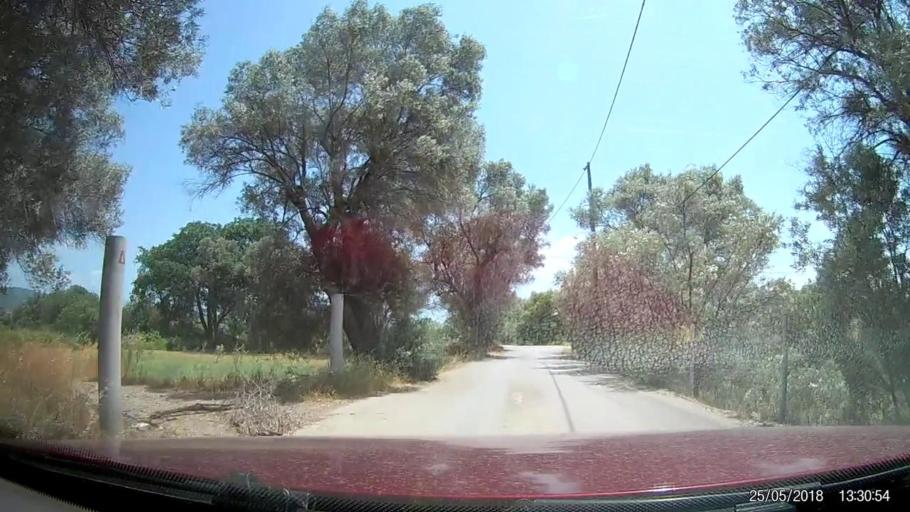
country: GR
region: Central Greece
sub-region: Nomos Evvoias
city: Mytikas
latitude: 38.4391
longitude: 23.6583
